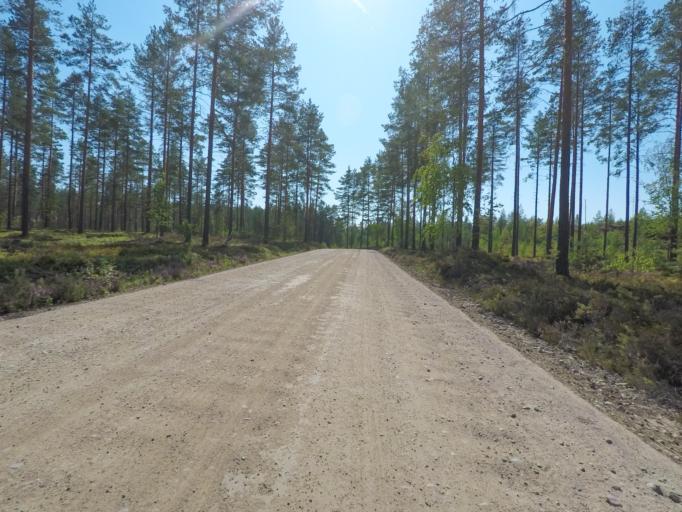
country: FI
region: Southern Savonia
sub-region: Mikkeli
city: Puumala
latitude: 61.4187
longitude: 28.0420
